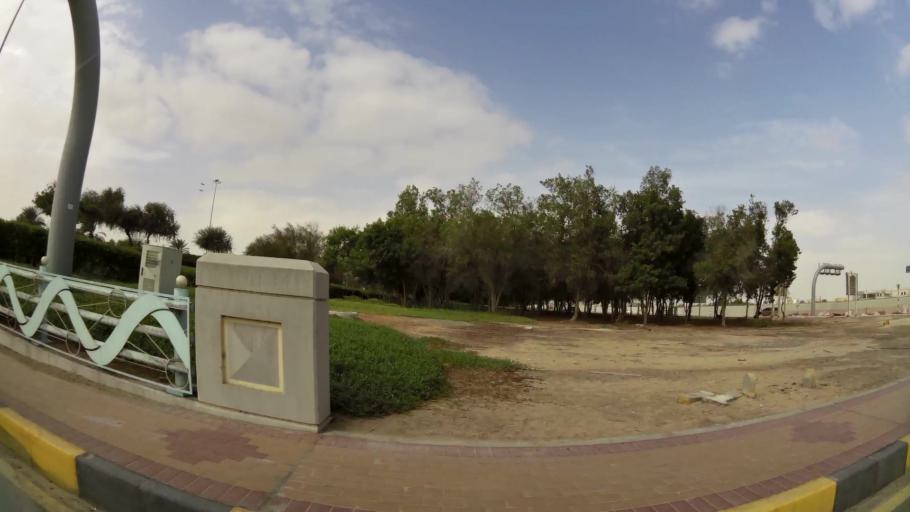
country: AE
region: Abu Dhabi
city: Abu Dhabi
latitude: 24.3996
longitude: 54.5028
